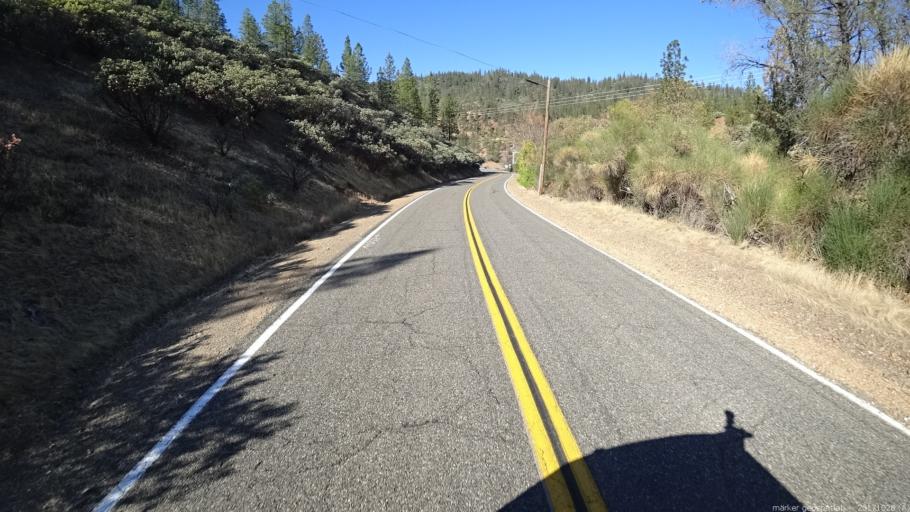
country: US
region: California
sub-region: Shasta County
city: Shasta
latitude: 40.6262
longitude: -122.4669
